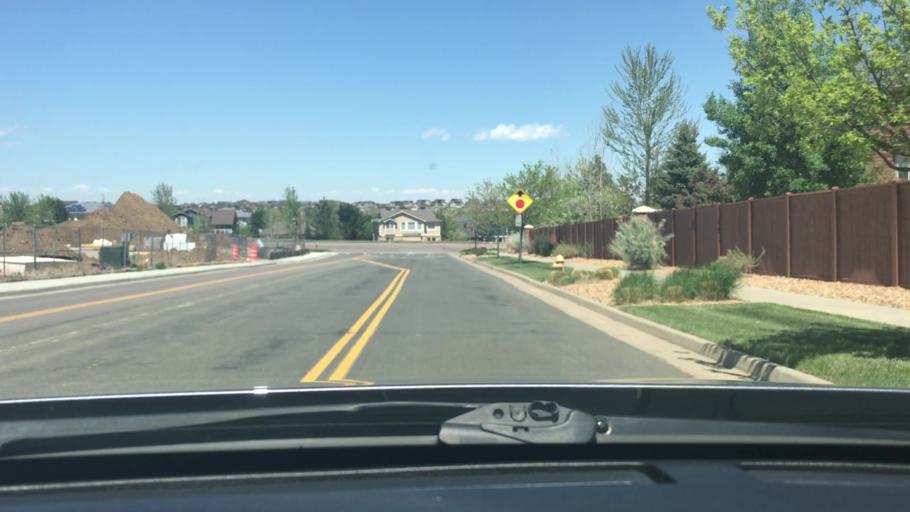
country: US
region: Colorado
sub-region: Arapahoe County
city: Dove Valley
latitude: 39.6519
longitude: -104.7438
